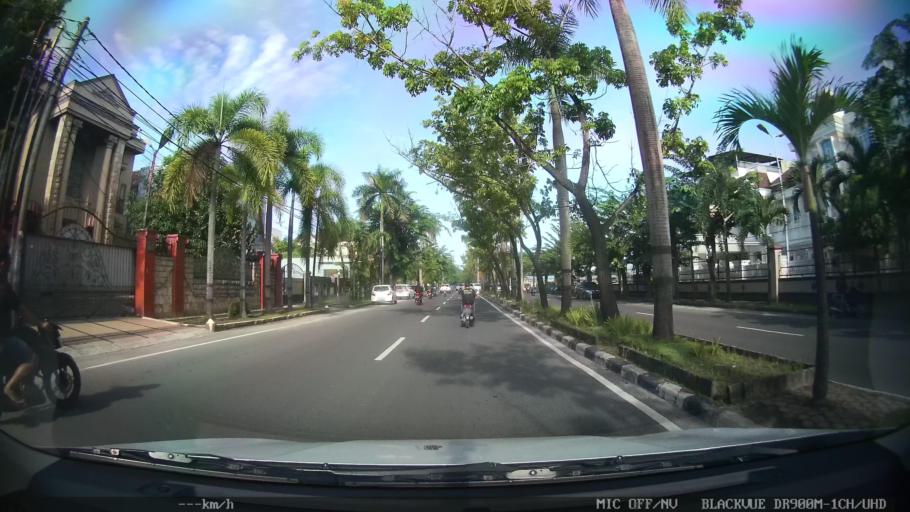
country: ID
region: North Sumatra
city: Medan
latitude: 3.6078
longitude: 98.6522
